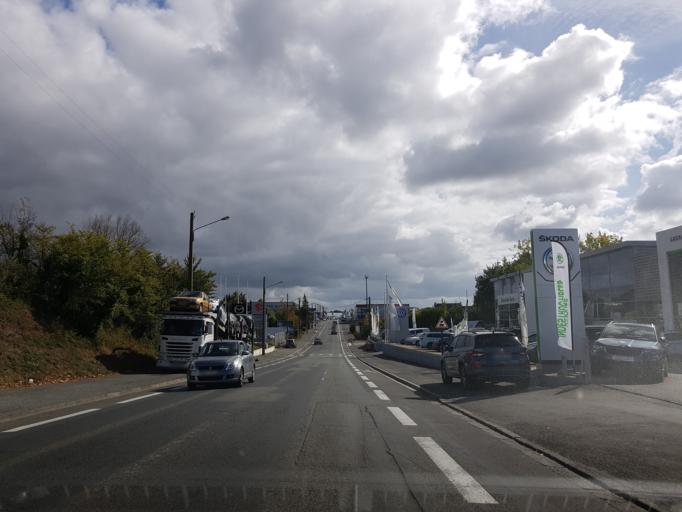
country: FR
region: Brittany
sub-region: Departement des Cotes-d'Armor
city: Langueux
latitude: 48.5116
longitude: -2.7368
